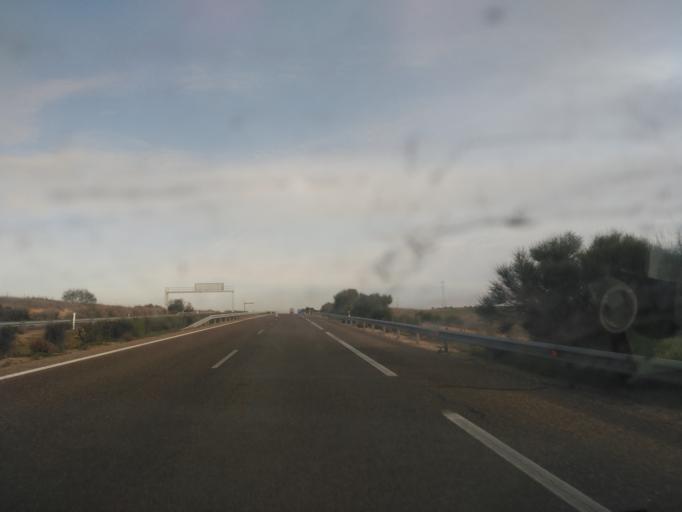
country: ES
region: Castille and Leon
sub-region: Provincia de Salamanca
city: Castellanos de Moriscos
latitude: 41.0042
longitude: -5.6076
